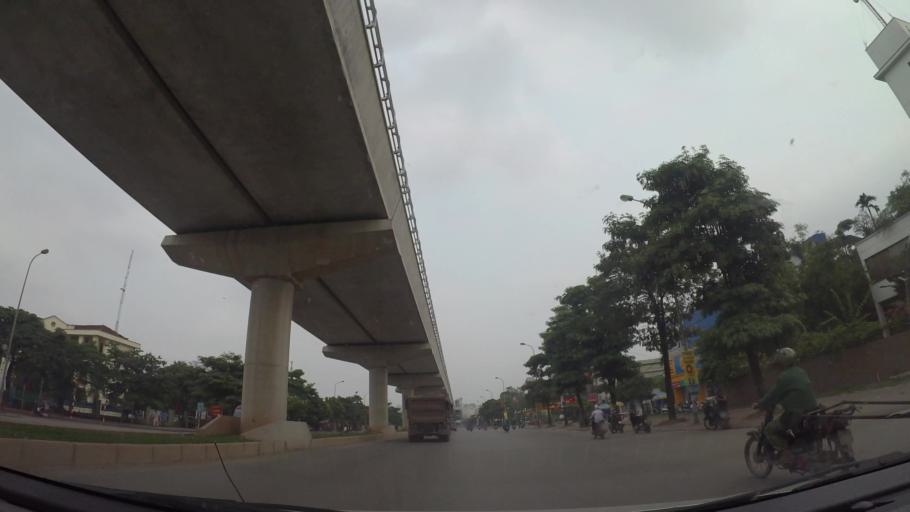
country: VN
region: Ha Noi
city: Cau Dien
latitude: 21.0492
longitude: 105.7416
